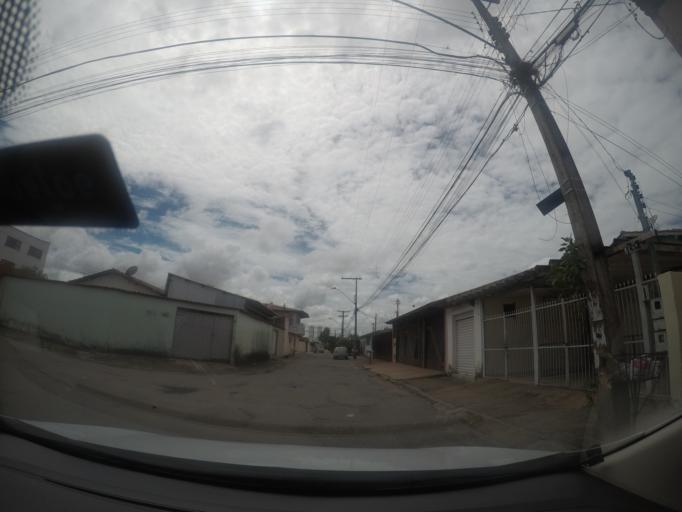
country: BR
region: Goias
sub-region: Goiania
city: Goiania
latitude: -16.6626
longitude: -49.3014
